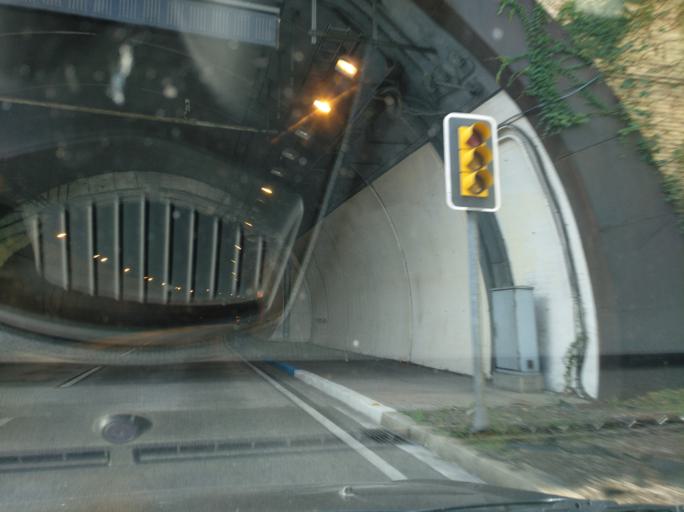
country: ES
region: Catalonia
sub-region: Provincia de Barcelona
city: Horta-Guinardo
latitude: 41.4138
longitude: 2.1667
